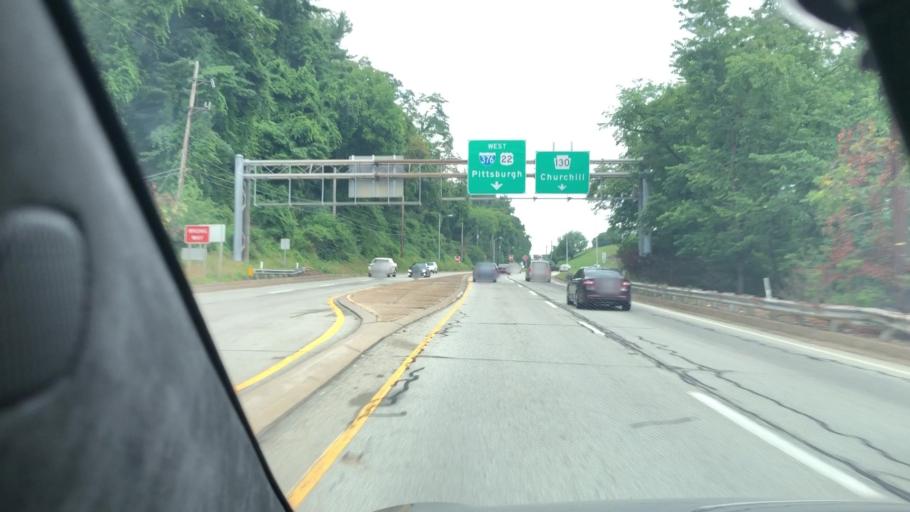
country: US
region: Pennsylvania
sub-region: Allegheny County
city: Churchill
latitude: 40.4388
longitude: -79.8316
